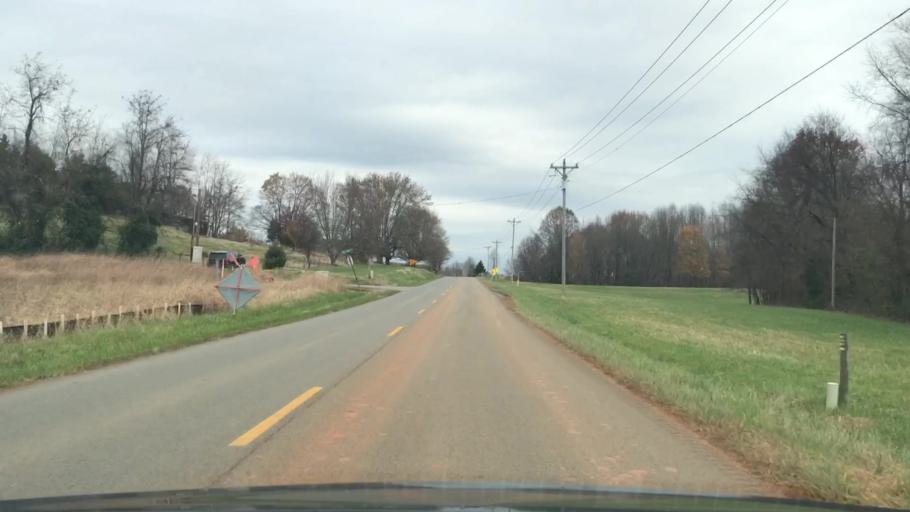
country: US
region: Kentucky
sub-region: Metcalfe County
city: Edmonton
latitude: 36.9074
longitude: -85.6512
